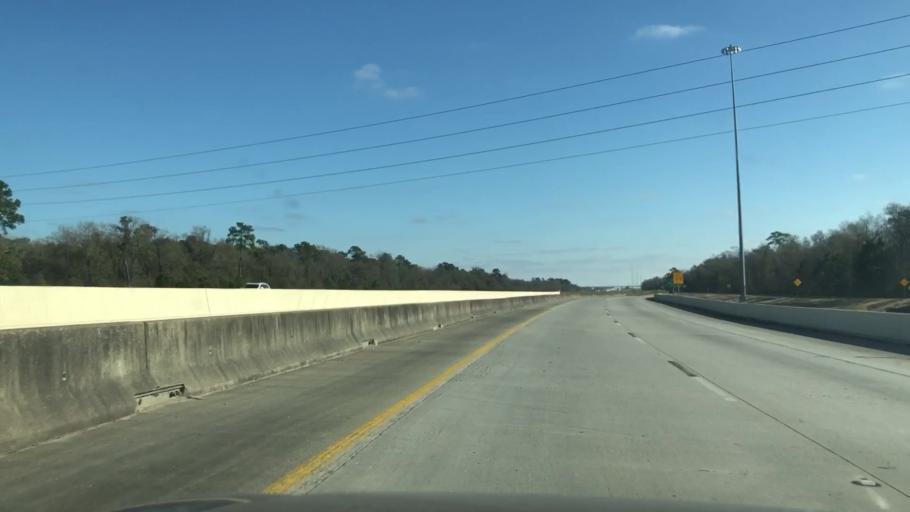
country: US
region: Texas
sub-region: Harris County
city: Cloverleaf
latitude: 29.8200
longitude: -95.2036
